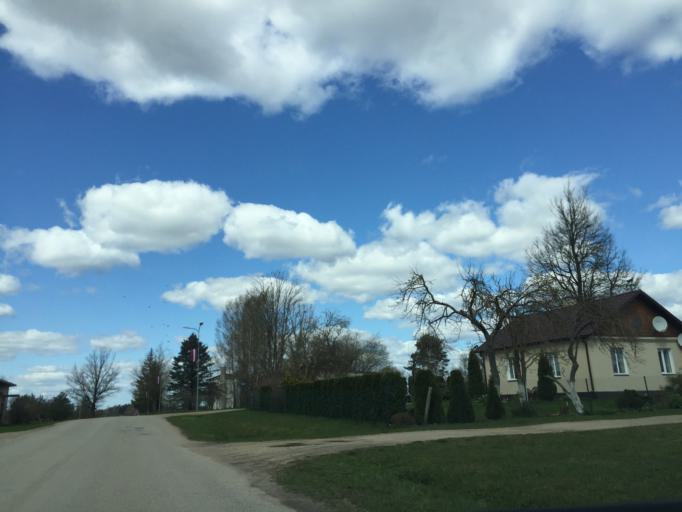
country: LV
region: Rezekne
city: Rezekne
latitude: 56.5630
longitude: 27.1425
